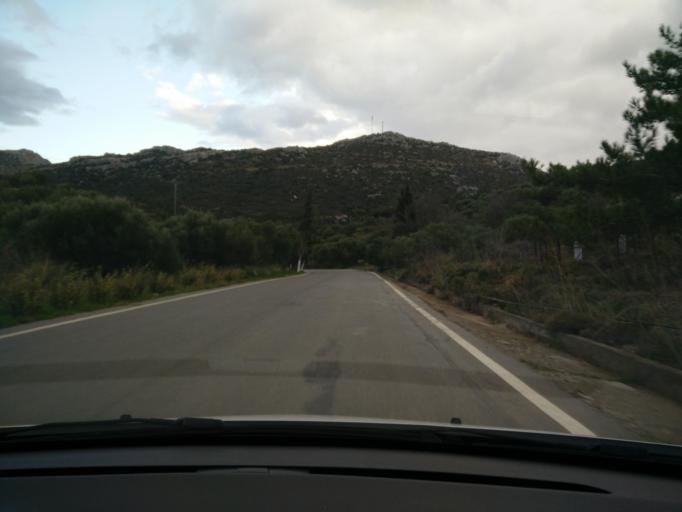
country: GR
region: Crete
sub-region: Nomos Lasithiou
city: Gra Liyia
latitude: 35.0843
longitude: 25.7086
